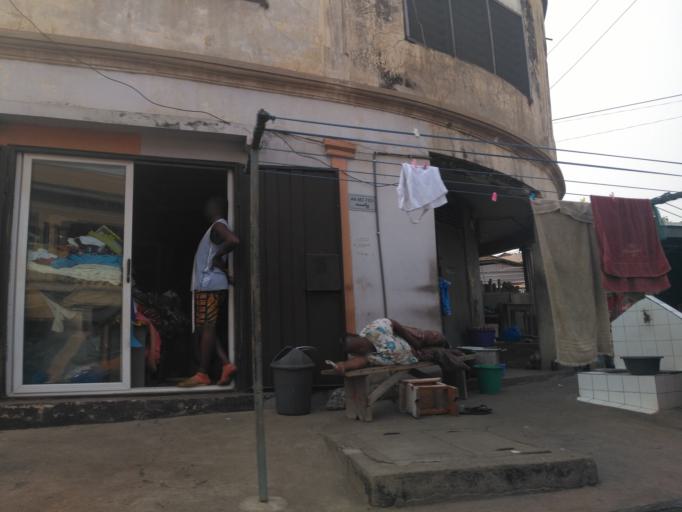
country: GH
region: Ashanti
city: Kumasi
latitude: 6.6867
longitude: -1.6090
